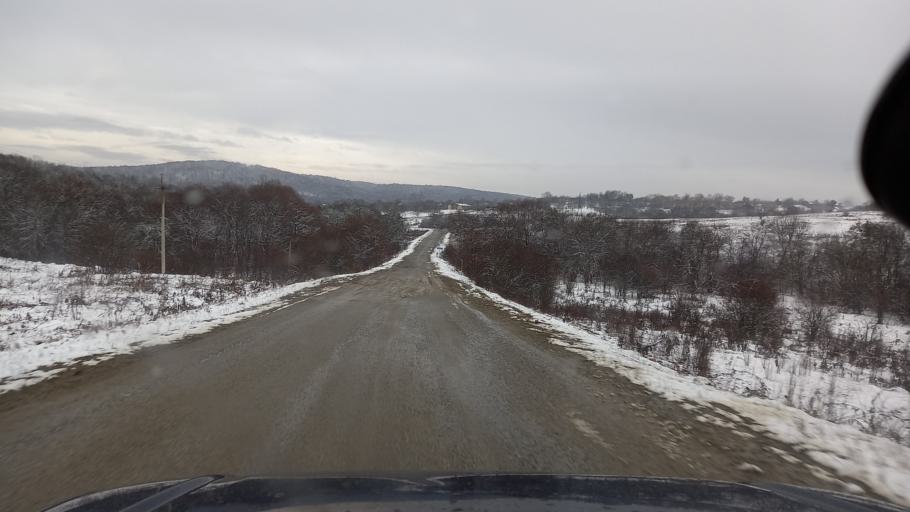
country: RU
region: Adygeya
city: Abadzekhskaya
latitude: 44.3593
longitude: 40.3961
